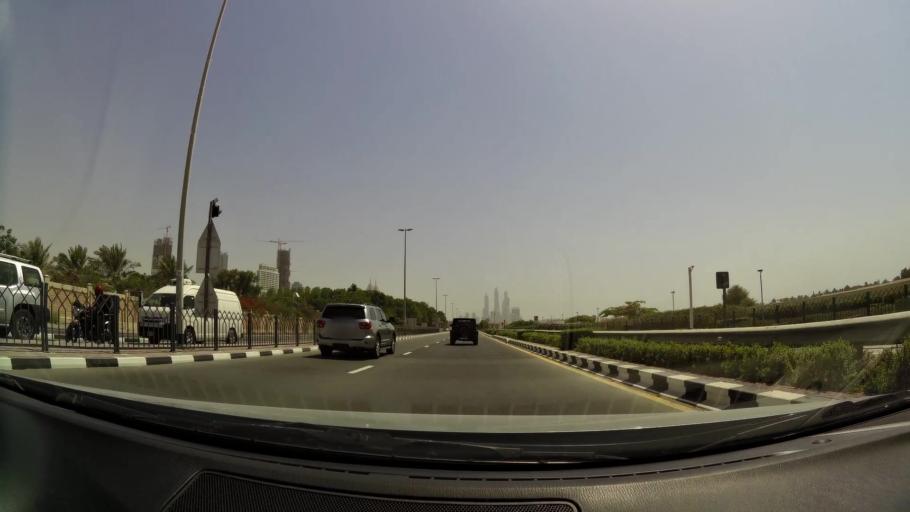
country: AE
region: Dubai
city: Dubai
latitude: 25.1187
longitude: 55.1799
